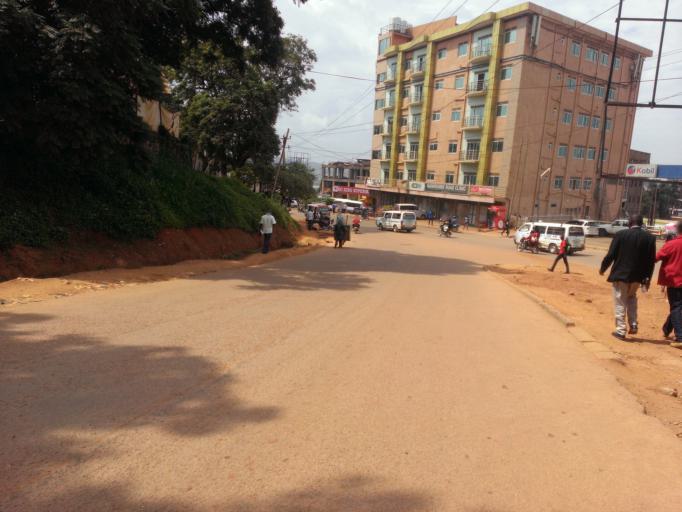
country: UG
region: Central Region
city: Kampala Central Division
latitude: 0.3138
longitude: 32.5678
